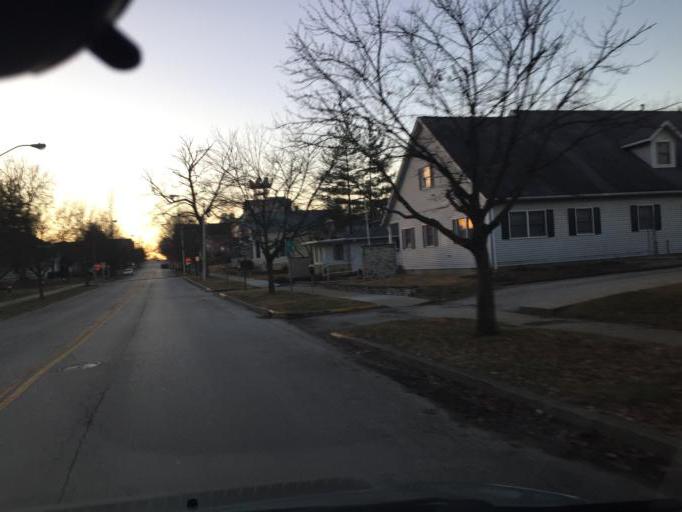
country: US
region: Indiana
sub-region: Monroe County
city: Bloomington
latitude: 39.1685
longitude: -86.5286
